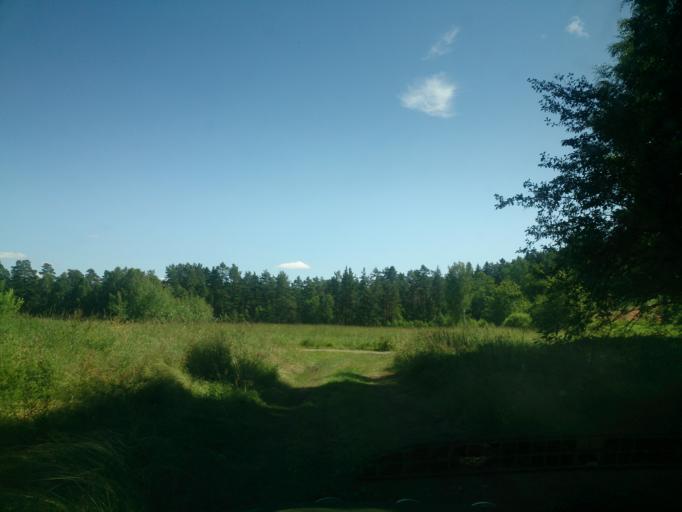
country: SE
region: OEstergoetland
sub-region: Atvidabergs Kommun
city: Atvidaberg
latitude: 58.2419
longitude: 15.9658
